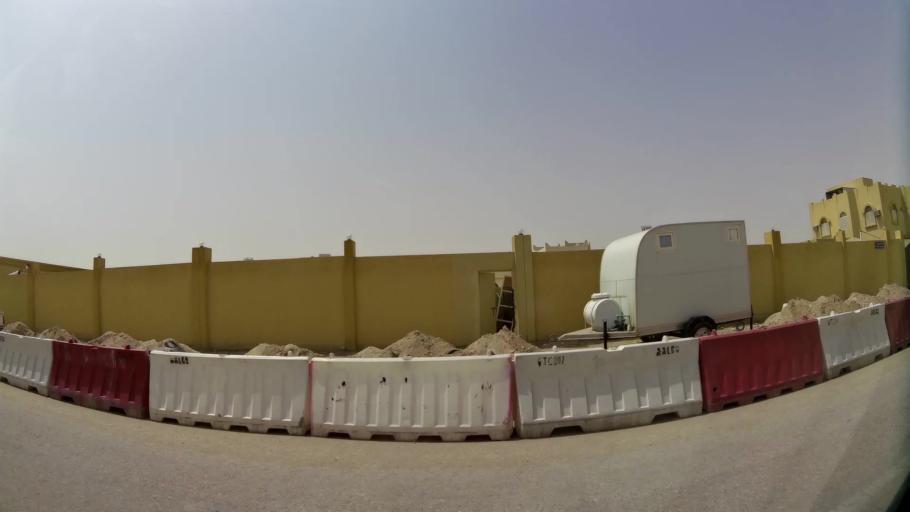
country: QA
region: Baladiyat ar Rayyan
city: Ar Rayyan
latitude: 25.2299
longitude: 51.4155
